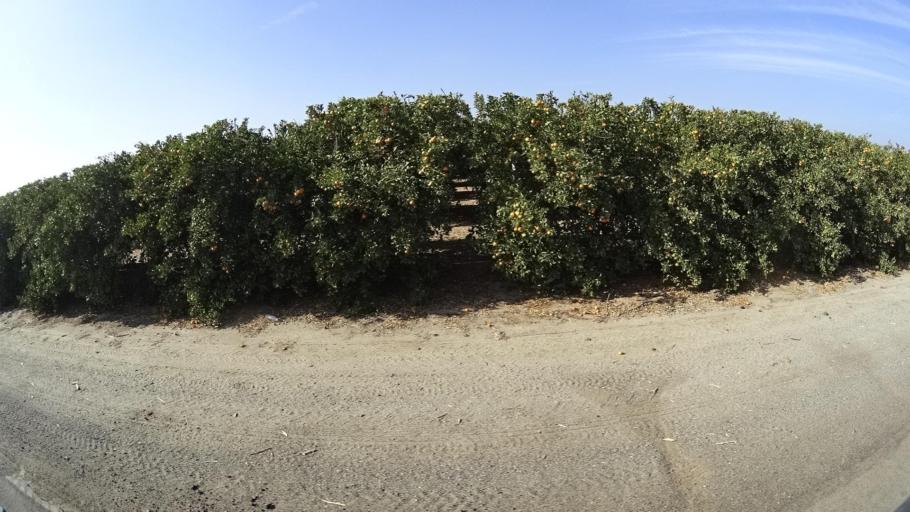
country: US
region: California
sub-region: Kern County
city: McFarland
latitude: 35.6357
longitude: -119.1335
